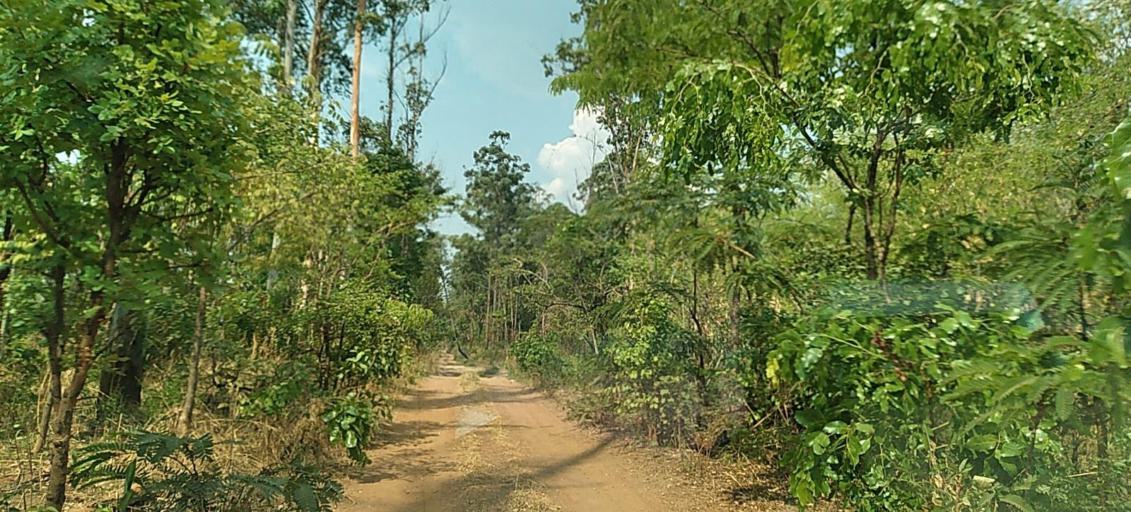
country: ZM
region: Copperbelt
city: Chingola
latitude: -12.7398
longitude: 27.7526
